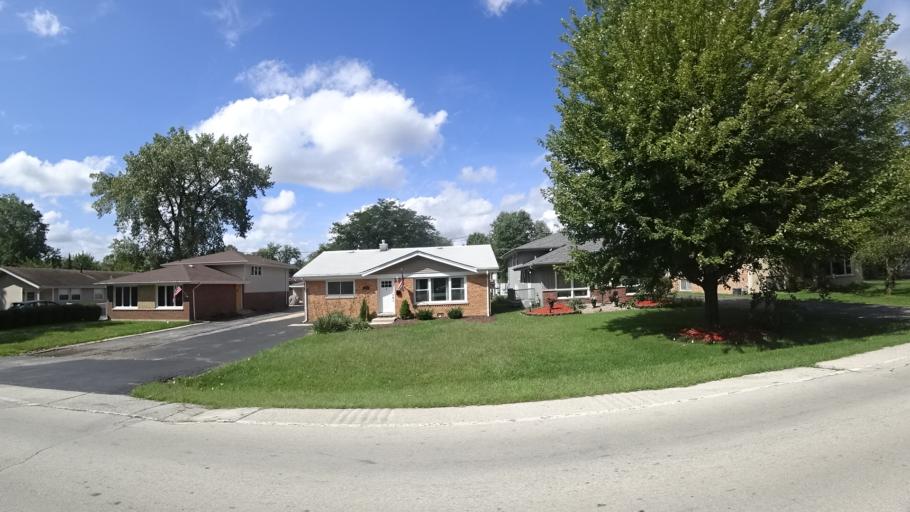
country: US
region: Illinois
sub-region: Cook County
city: Tinley Park
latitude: 41.5687
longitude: -87.7744
